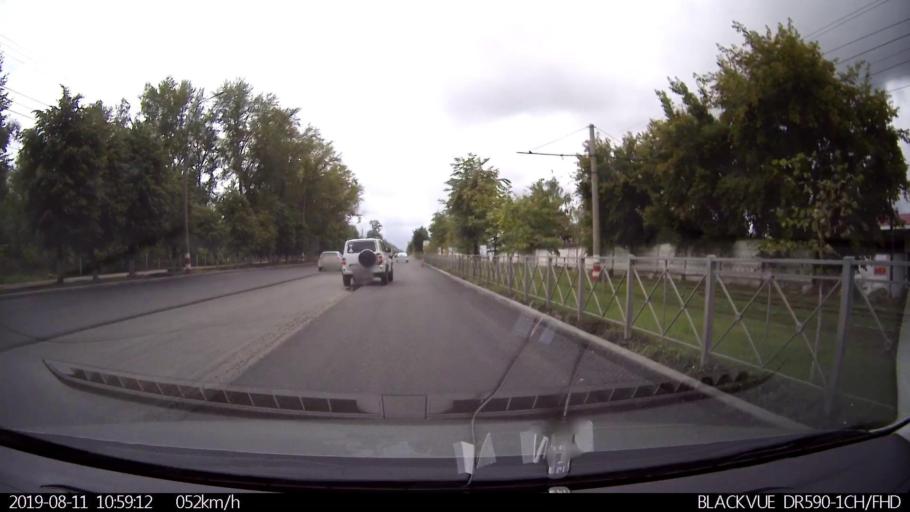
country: RU
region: Ulyanovsk
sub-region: Ulyanovskiy Rayon
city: Ulyanovsk
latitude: 54.2518
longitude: 48.3167
